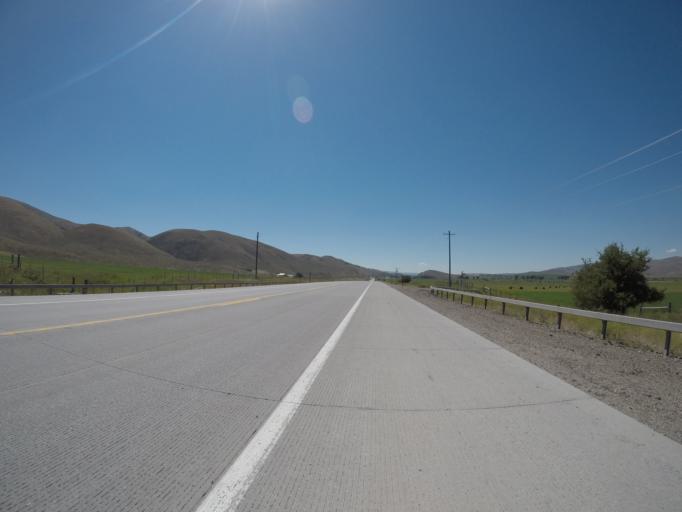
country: US
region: Idaho
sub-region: Bear Lake County
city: Montpelier
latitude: 42.1570
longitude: -110.9838
